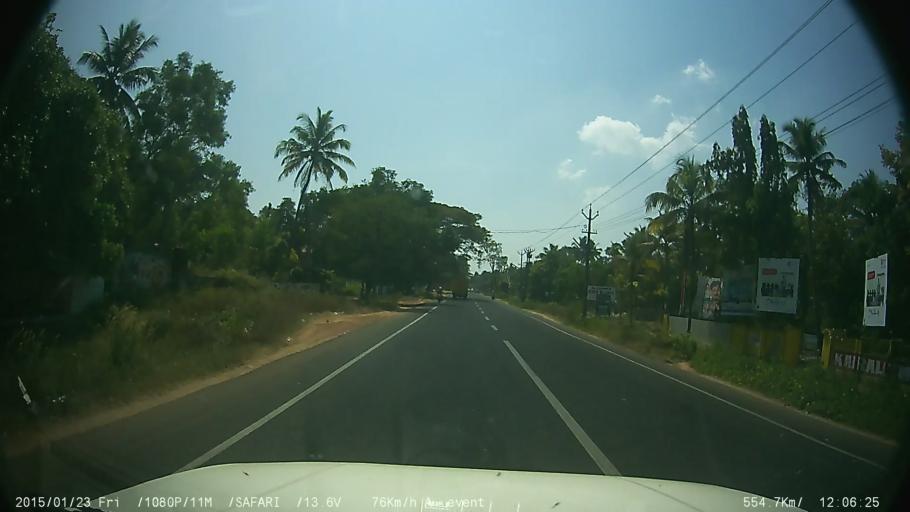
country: IN
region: Kerala
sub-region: Alappuzha
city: Shertallai
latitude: 9.5973
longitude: 76.3280
